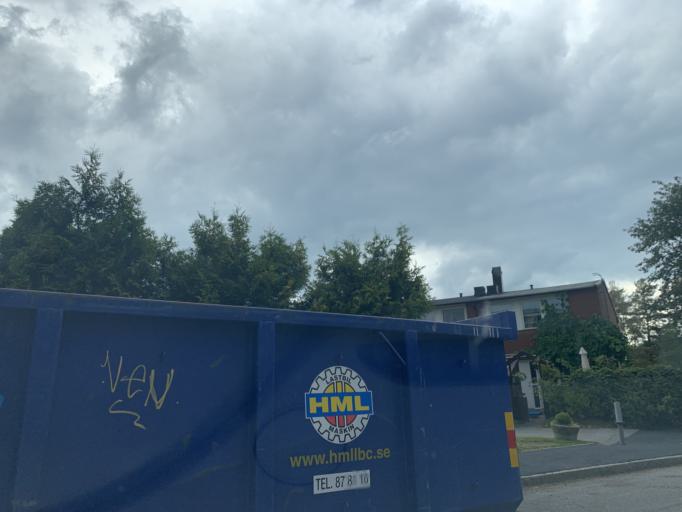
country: SE
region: Vaestra Goetaland
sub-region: Goteborg
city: Hammarkullen
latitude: 57.7757
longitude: 12.0378
